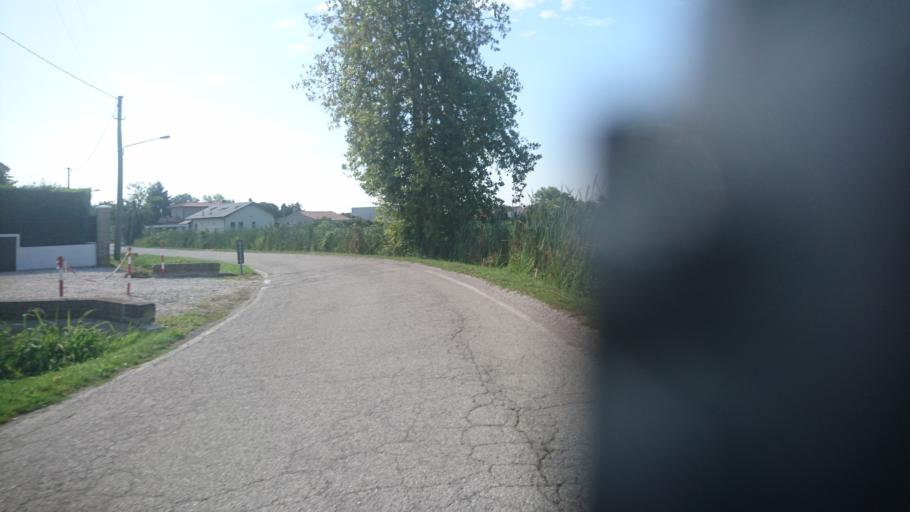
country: IT
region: Veneto
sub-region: Provincia di Padova
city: Mandriola-Sant'Agostino
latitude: 45.3737
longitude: 11.8378
